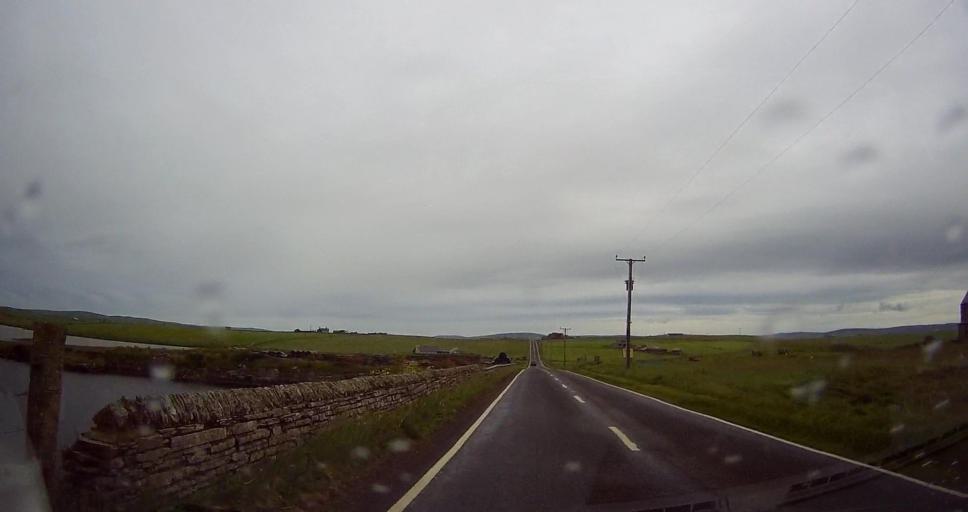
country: GB
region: Scotland
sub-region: Orkney Islands
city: Stromness
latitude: 59.0245
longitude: -3.2952
